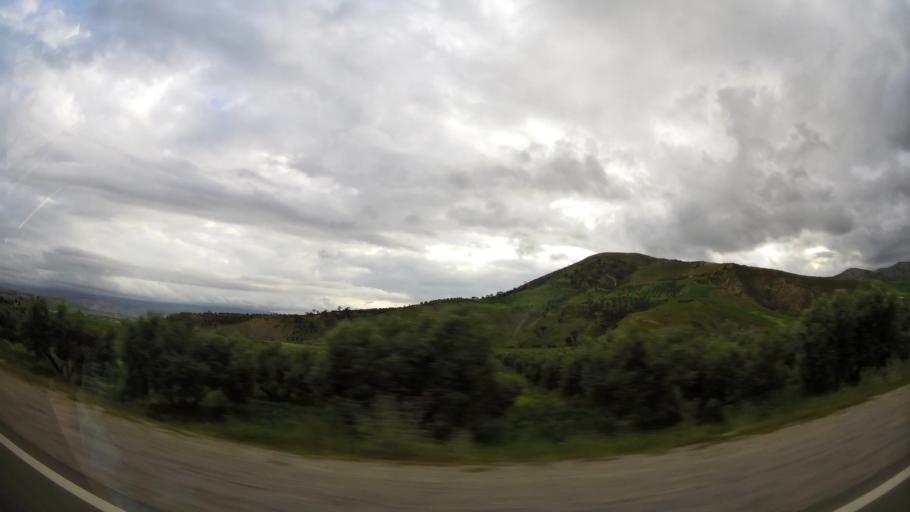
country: MA
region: Taza-Al Hoceima-Taounate
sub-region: Taza
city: Taza
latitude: 34.2831
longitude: -3.9592
